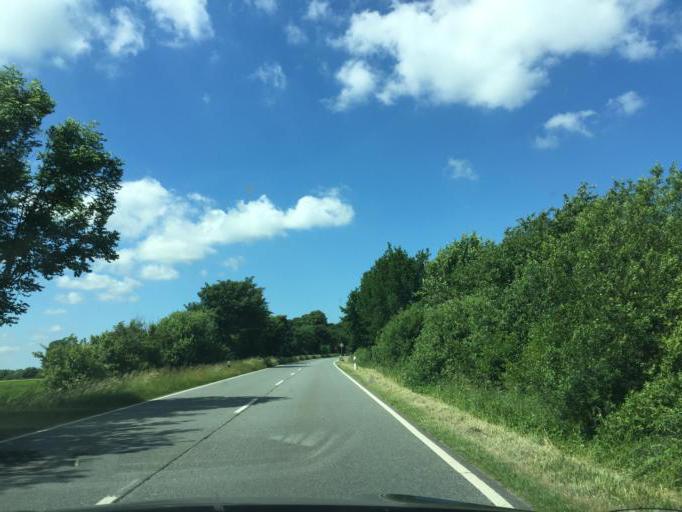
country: DE
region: Schleswig-Holstein
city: Harrislee
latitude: 54.7825
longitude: 9.3755
